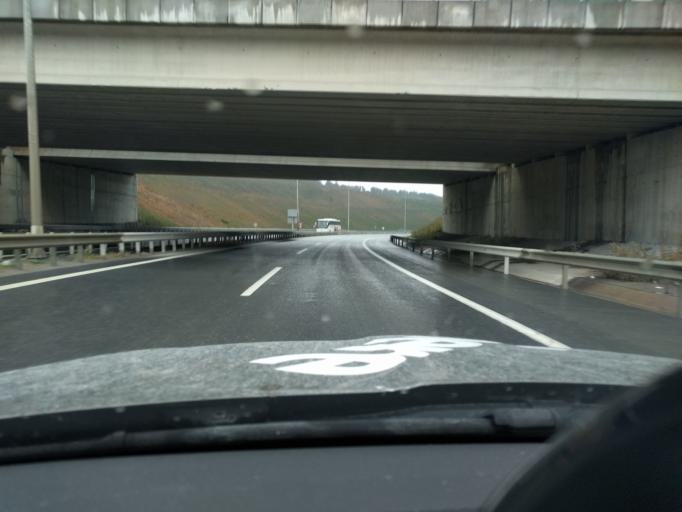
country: TR
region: Istanbul
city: Kemerburgaz
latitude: 41.2113
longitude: 28.8269
